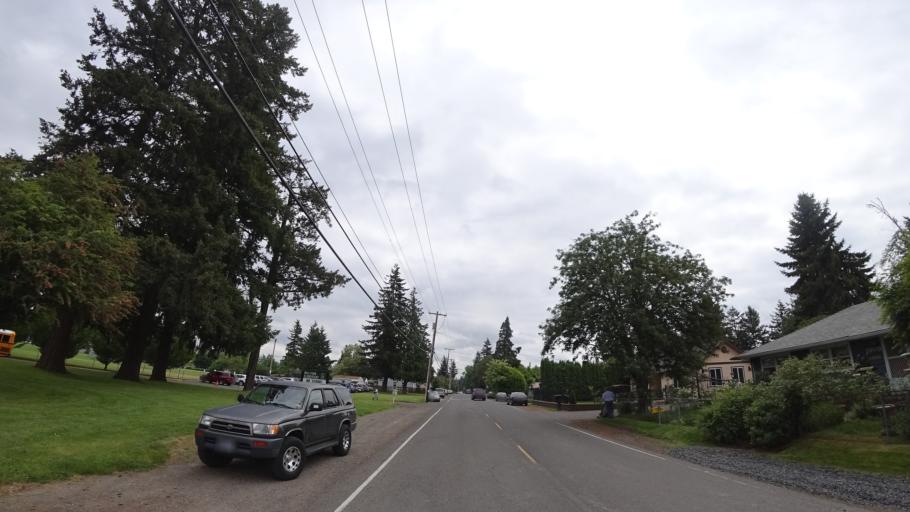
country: US
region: Oregon
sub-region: Multnomah County
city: Lents
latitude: 45.5096
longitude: -122.5428
